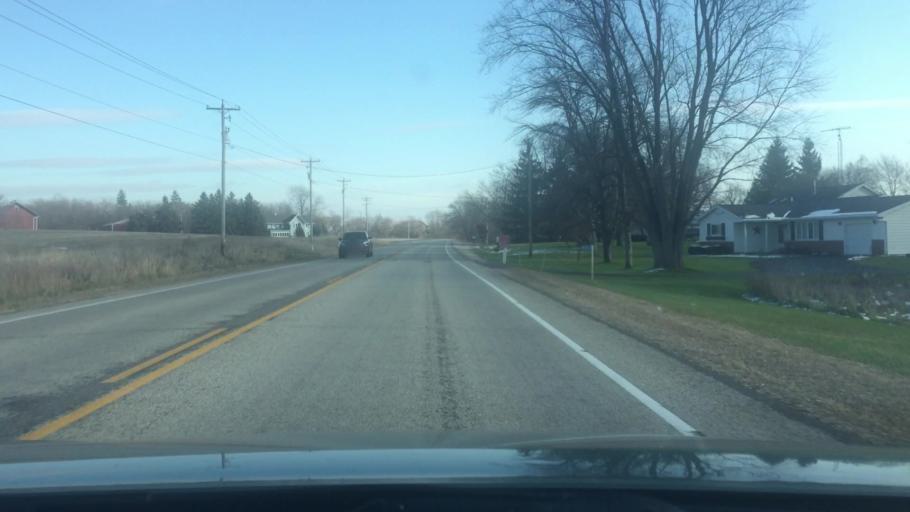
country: US
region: Wisconsin
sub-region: Walworth County
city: Whitewater
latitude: 42.9326
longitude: -88.7244
